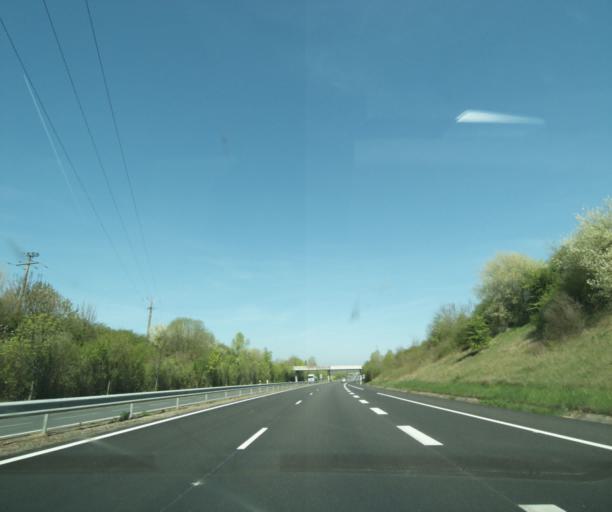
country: FR
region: Bourgogne
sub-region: Departement de la Nievre
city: La Charite-sur-Loire
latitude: 47.1381
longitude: 3.0434
